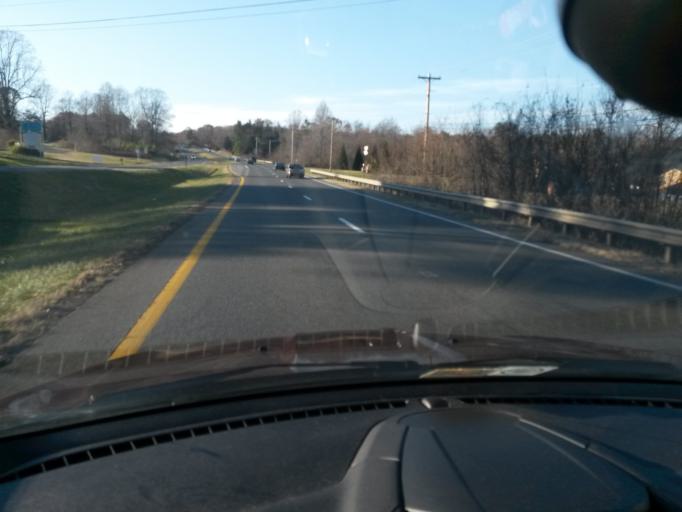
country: US
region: Virginia
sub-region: Campbell County
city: Concord
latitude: 37.3715
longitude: -79.0196
